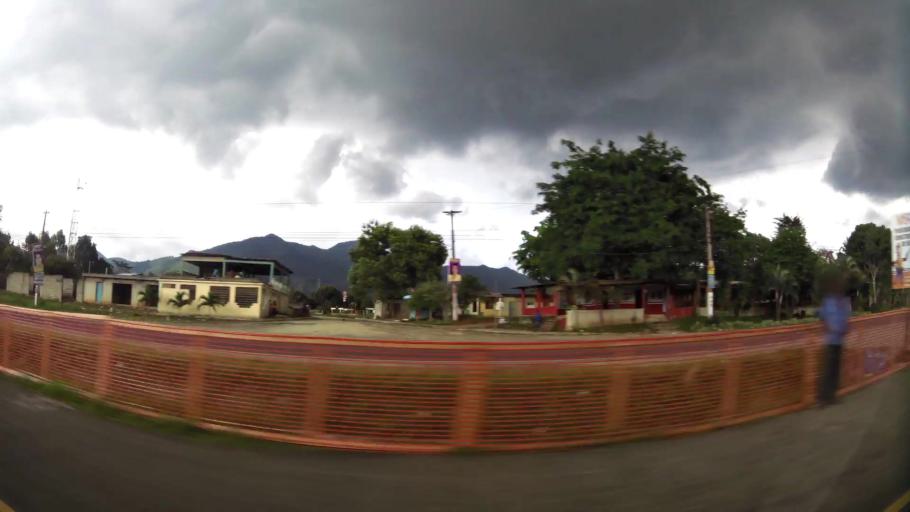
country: DO
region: San Cristobal
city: Villa Altagracia
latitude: 18.7511
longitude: -70.2341
